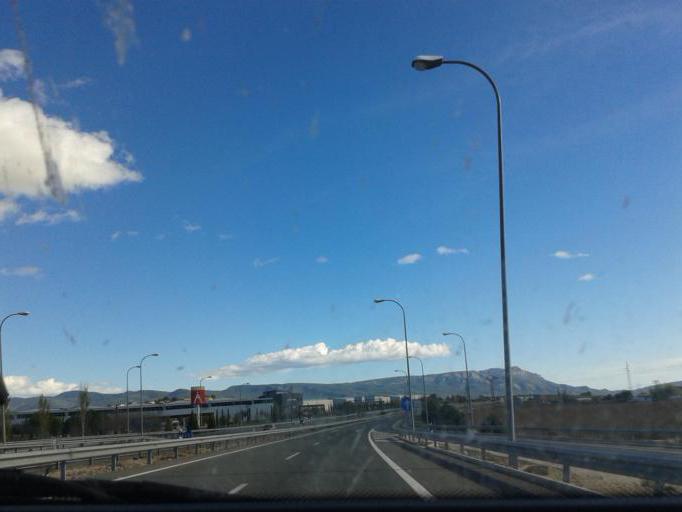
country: ES
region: Valencia
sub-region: Provincia de Alicante
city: Castalla
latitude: 38.6080
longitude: -0.6667
